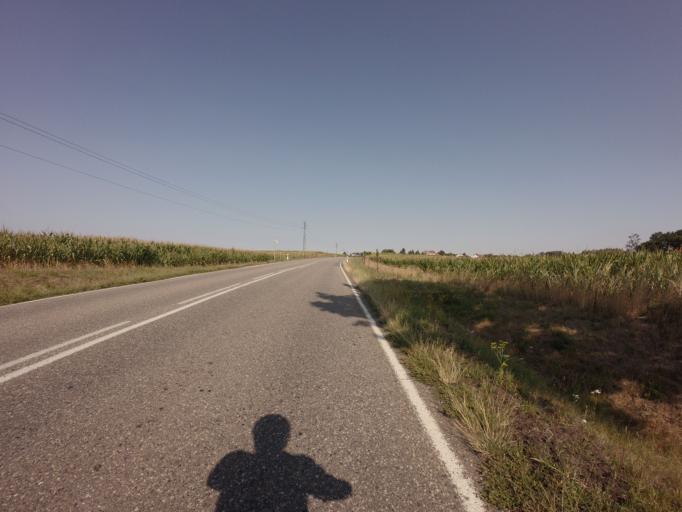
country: CZ
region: Central Bohemia
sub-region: Okres Benesov
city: Benesov
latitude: 49.7970
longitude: 14.6584
